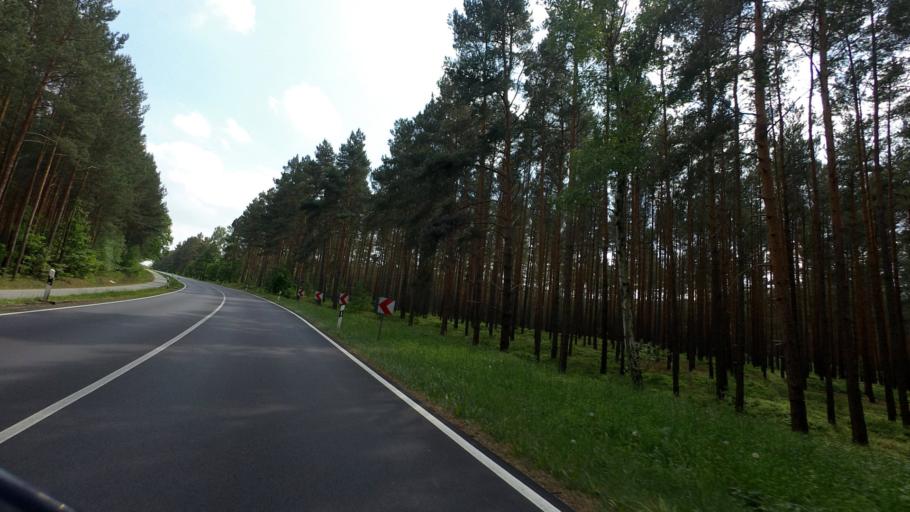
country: DE
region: Saxony
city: Niesky
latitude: 51.3258
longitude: 14.8198
